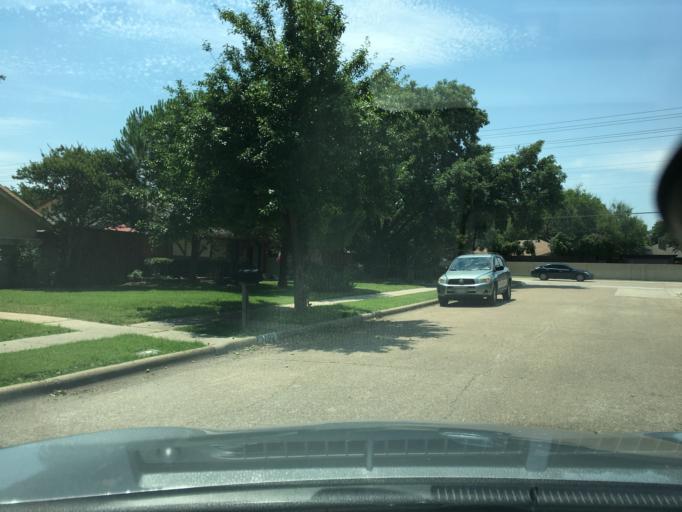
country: US
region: Texas
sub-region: Dallas County
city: Richardson
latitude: 32.9611
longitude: -96.6875
